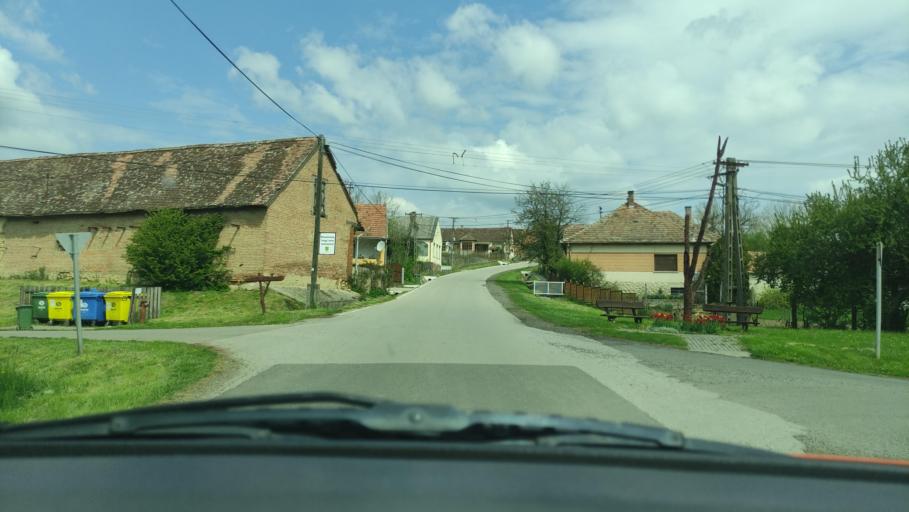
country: HU
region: Baranya
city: Sasd
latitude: 46.2864
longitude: 18.1017
